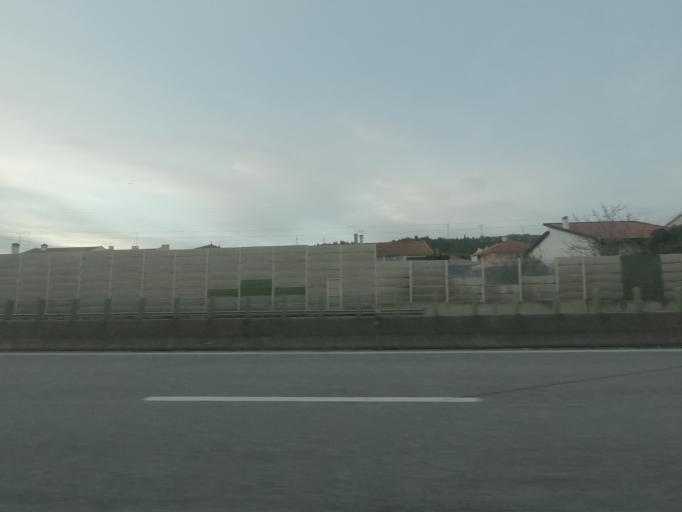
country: PT
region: Lisbon
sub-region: Vila Franca de Xira
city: Sobralinho
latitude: 38.9159
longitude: -9.0236
